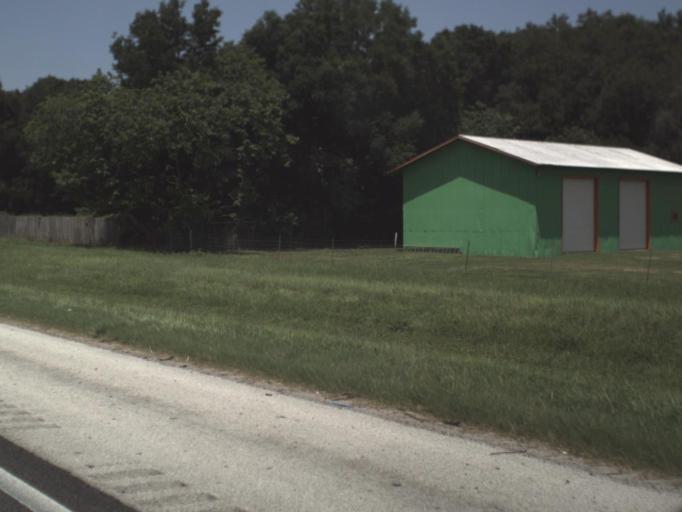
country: US
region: Florida
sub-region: Hillsborough County
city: Dover
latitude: 28.0274
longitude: -82.1990
